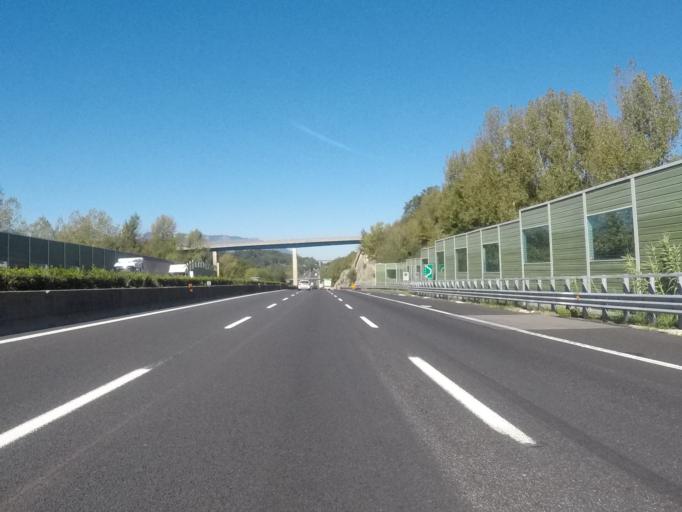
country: IT
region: Latium
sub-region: Provincia di Frosinone
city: Arnara
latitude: 41.5729
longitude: 13.3774
